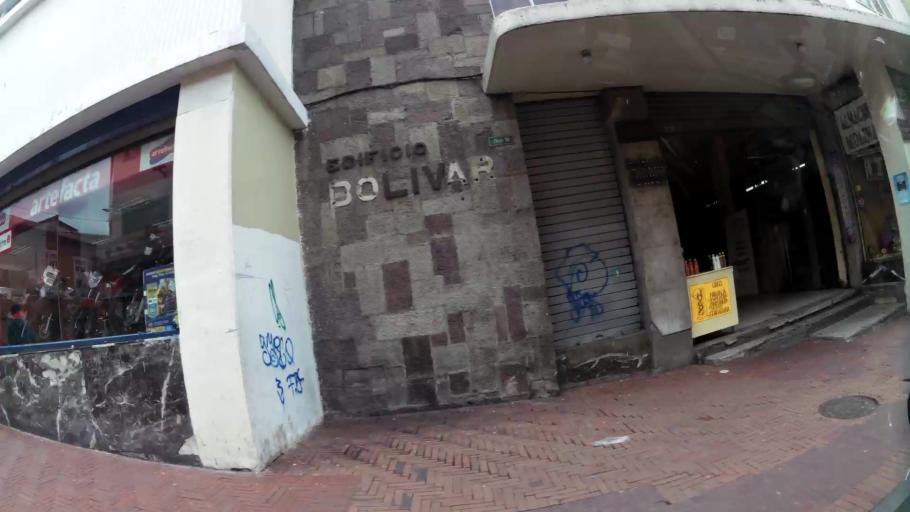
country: EC
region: Pichincha
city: Quito
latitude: -0.2227
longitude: -78.5133
